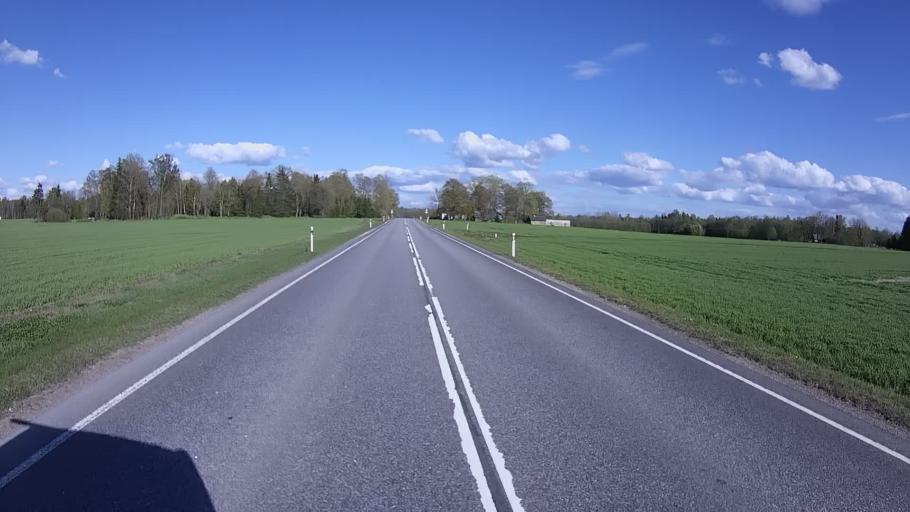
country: EE
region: Viljandimaa
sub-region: Vohma linn
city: Vohma
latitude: 58.6323
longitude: 25.7155
